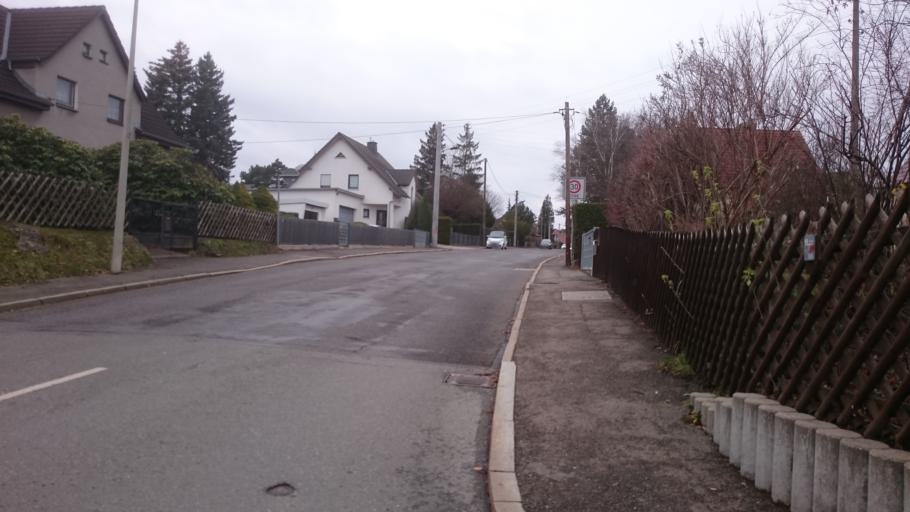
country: DE
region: Saxony
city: Weissenborn
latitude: 50.7410
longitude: 12.4721
